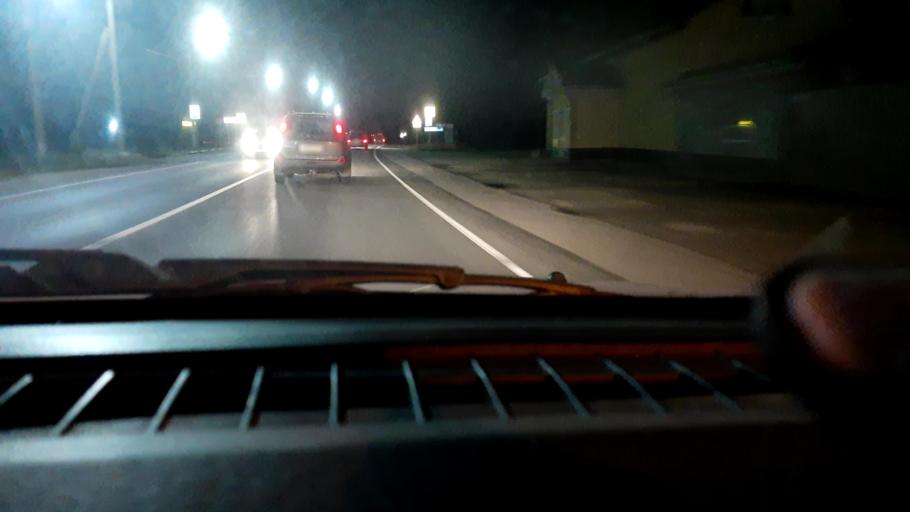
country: RU
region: Nizjnij Novgorod
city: Sitniki
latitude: 56.5437
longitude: 44.0190
